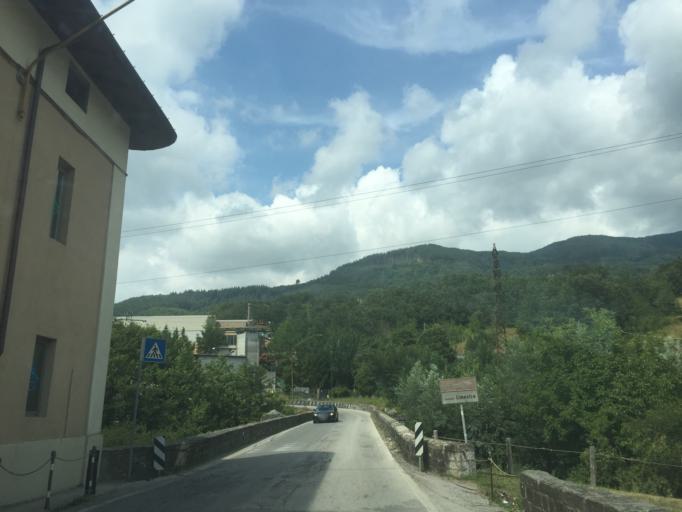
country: IT
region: Tuscany
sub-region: Provincia di Pistoia
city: San Marcello Pistoiese
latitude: 44.0475
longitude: 10.8084
